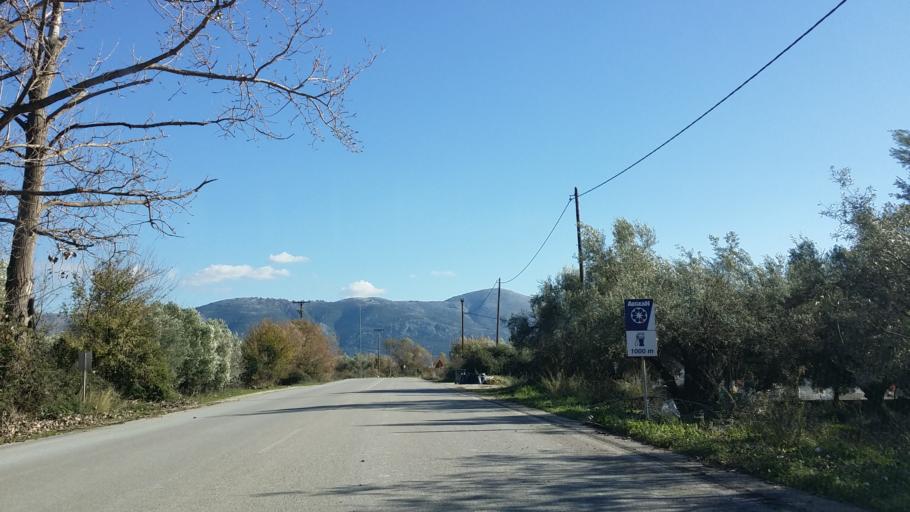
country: GR
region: West Greece
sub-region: Nomos Aitolias kai Akarnanias
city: Kandila
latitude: 38.6775
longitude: 20.9375
